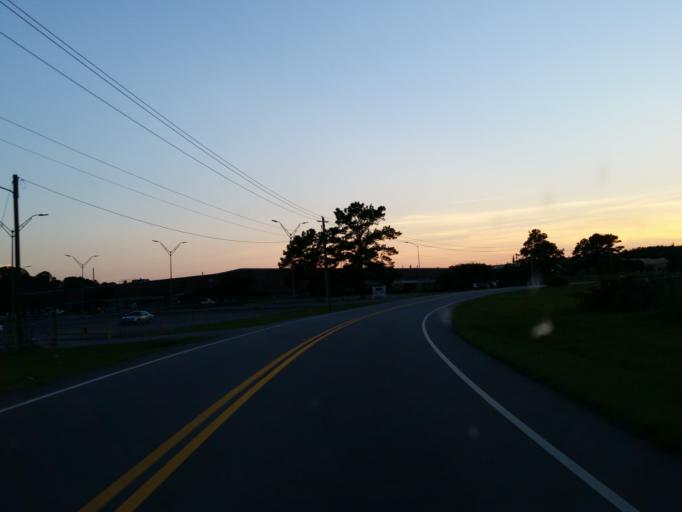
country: US
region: Georgia
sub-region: Tift County
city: Unionville
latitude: 31.4136
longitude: -83.4821
